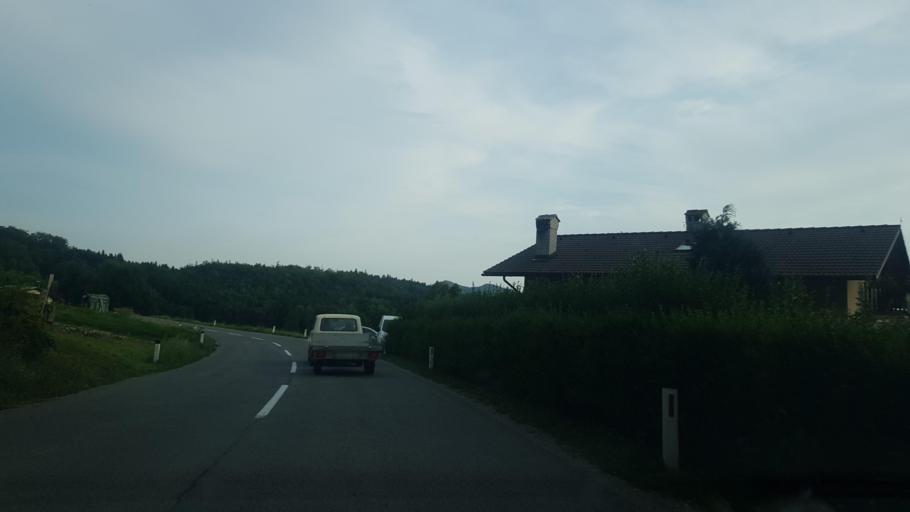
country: SI
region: Vipava
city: Vipava
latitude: 45.8654
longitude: 14.0604
